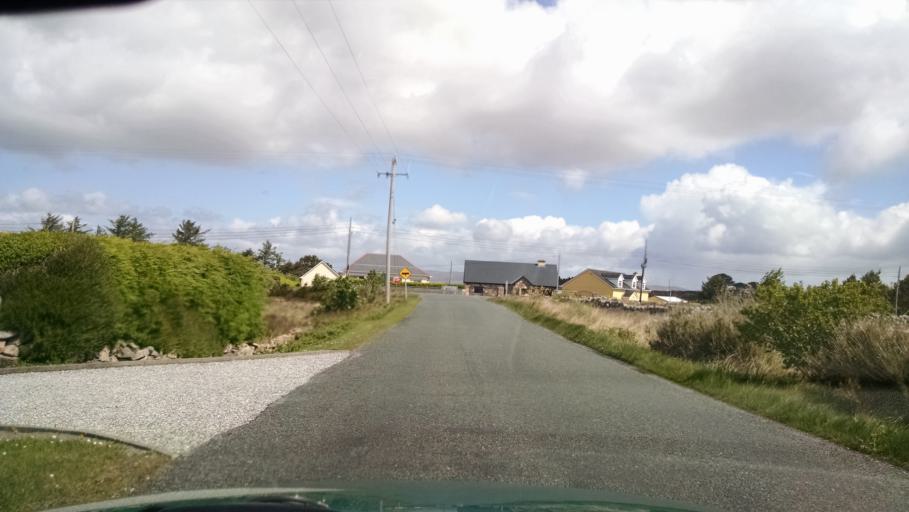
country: IE
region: Connaught
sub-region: County Galway
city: Oughterard
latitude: 53.3001
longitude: -9.5784
